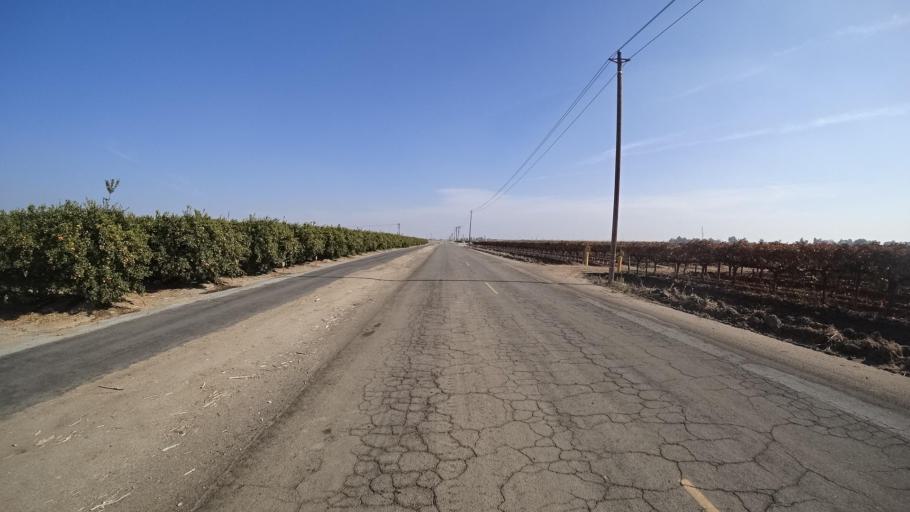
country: US
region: California
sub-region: Kern County
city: Greenacres
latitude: 35.5299
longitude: -119.1183
